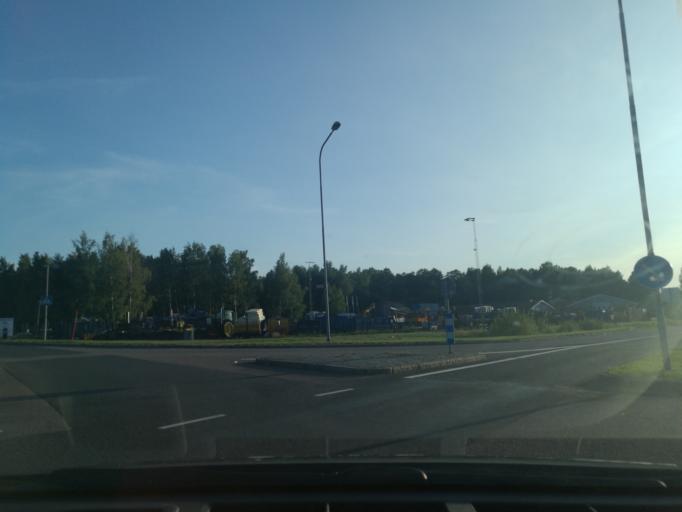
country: SE
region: Vaestmanland
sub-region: Vasteras
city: Vasteras
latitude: 59.6185
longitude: 16.5055
